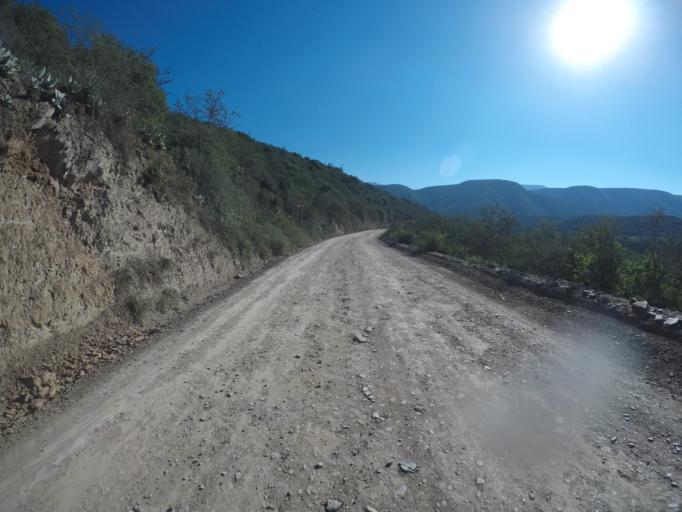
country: ZA
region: Eastern Cape
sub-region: Cacadu District Municipality
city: Kruisfontein
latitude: -33.6669
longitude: 24.5676
